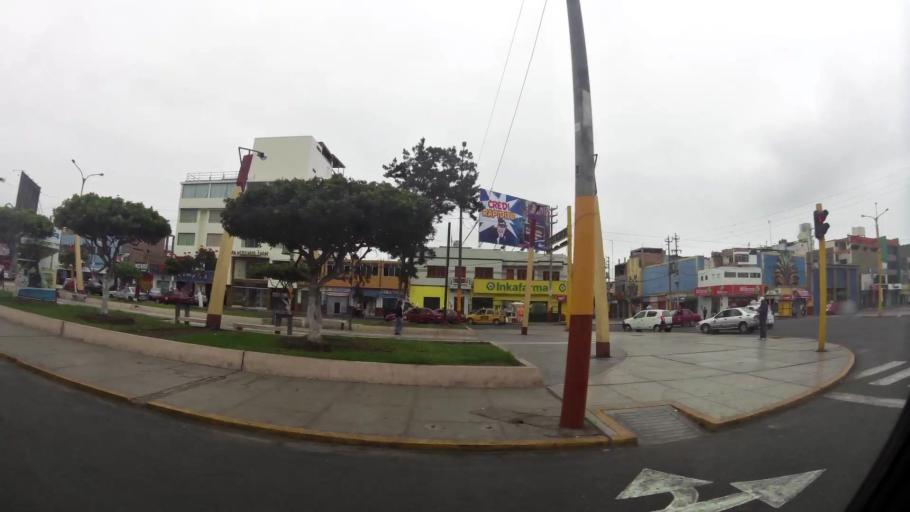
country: PE
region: Ancash
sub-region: Provincia de Santa
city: Chimbote
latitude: -9.0759
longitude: -78.5910
